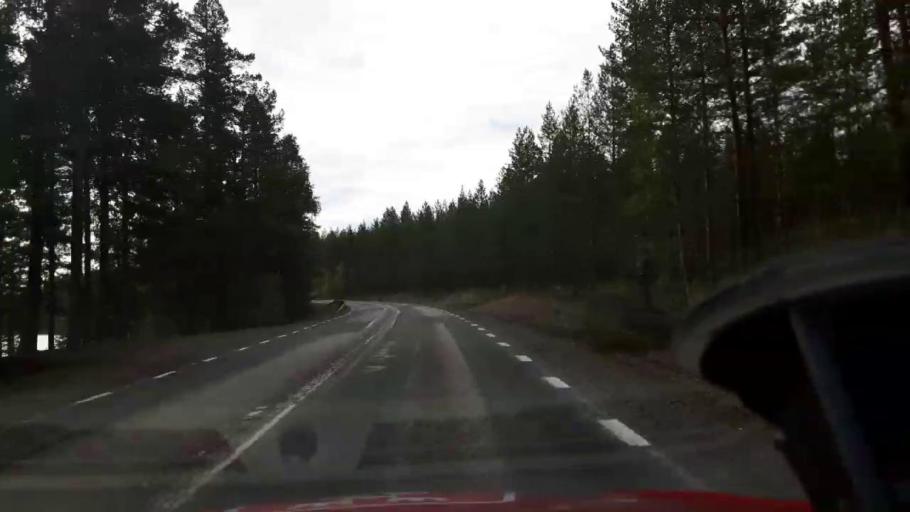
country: SE
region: Gaevleborg
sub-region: Ljusdals Kommun
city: Farila
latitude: 61.9602
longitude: 15.3575
